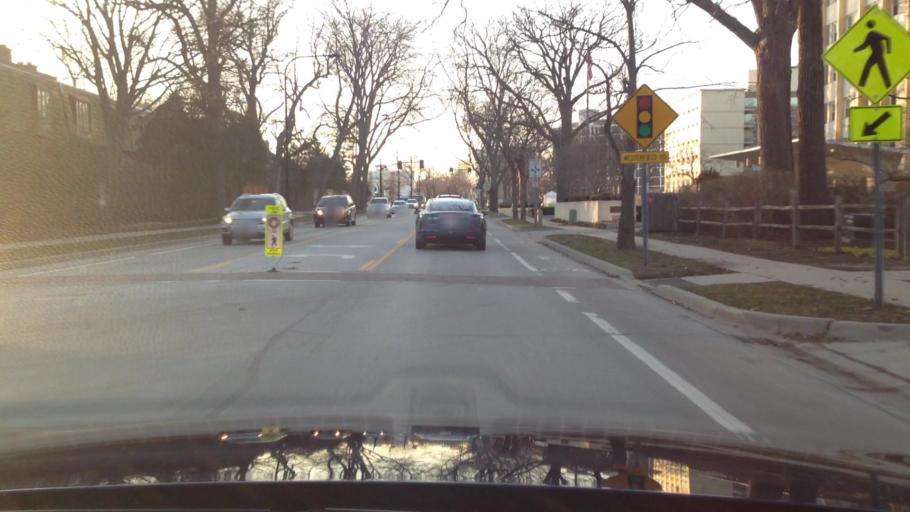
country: US
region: Illinois
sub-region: Cook County
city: Kenilworth
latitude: 42.0852
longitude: -87.6982
